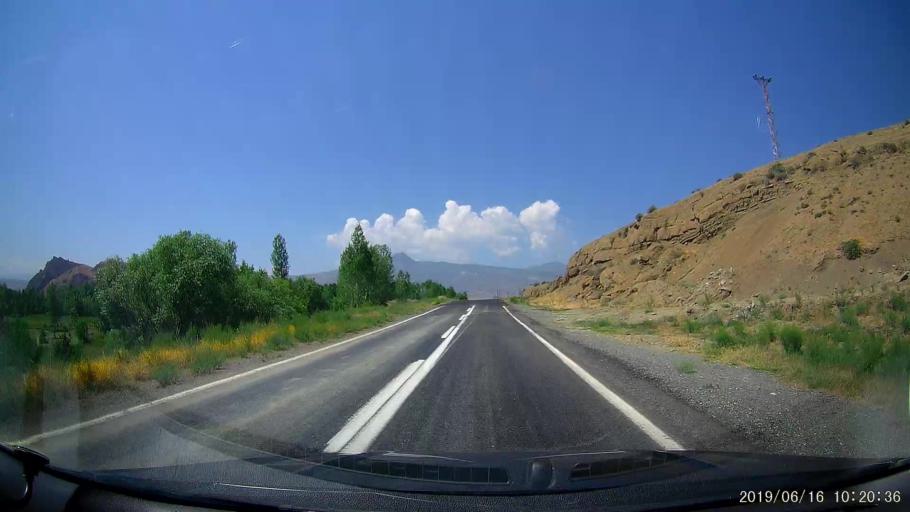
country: TR
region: Igdir
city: Tuzluca
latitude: 40.1463
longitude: 43.6461
